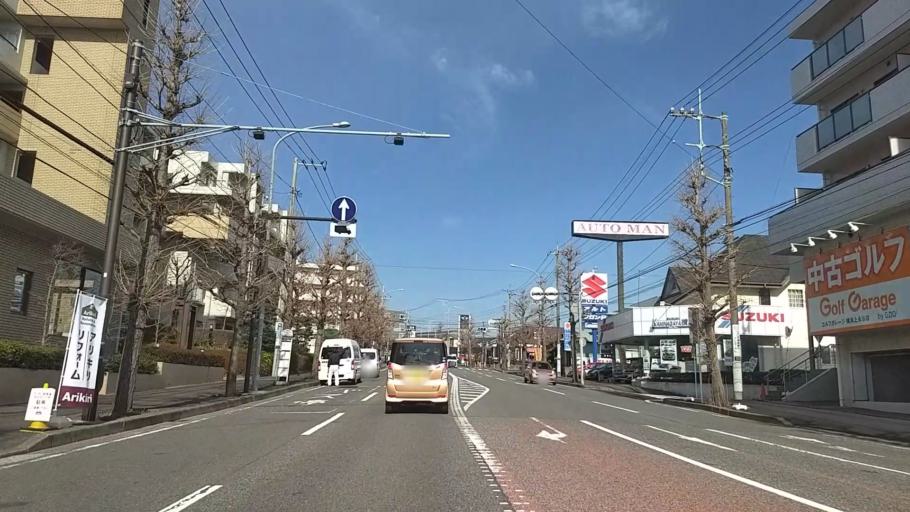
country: JP
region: Kanagawa
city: Kamakura
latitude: 35.3961
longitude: 139.5649
